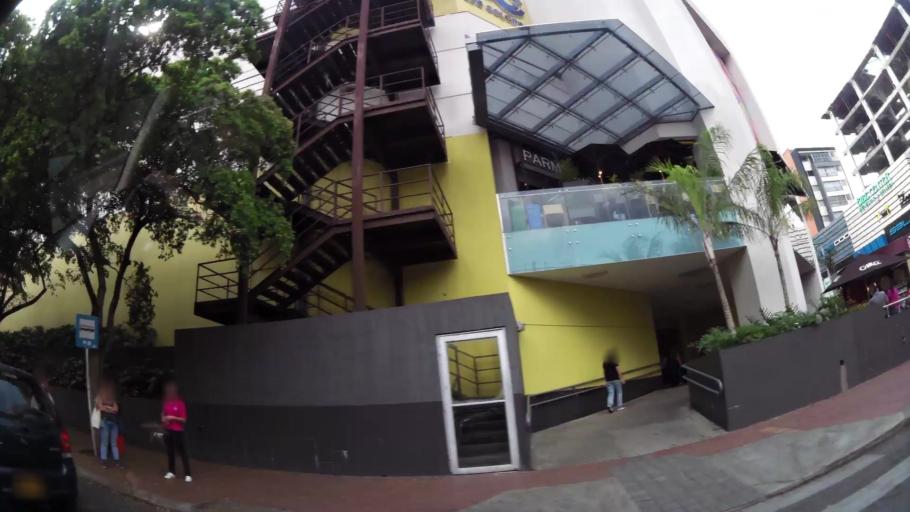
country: CO
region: Antioquia
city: Medellin
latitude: 6.2407
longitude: -75.5862
